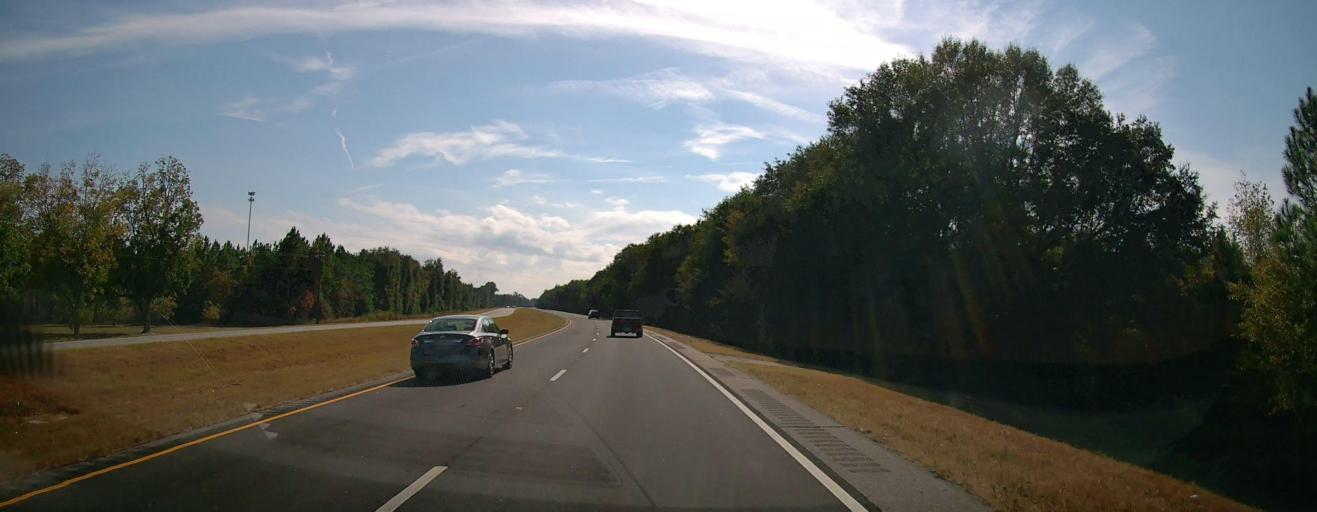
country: US
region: Georgia
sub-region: Dougherty County
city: Putney
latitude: 31.4008
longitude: -84.1454
